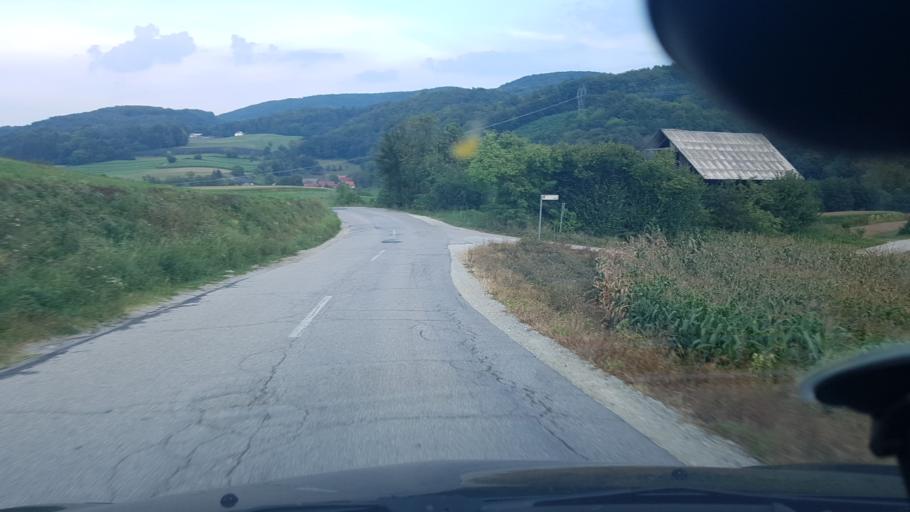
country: SI
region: Kozje
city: Kozje
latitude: 46.0297
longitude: 15.5525
